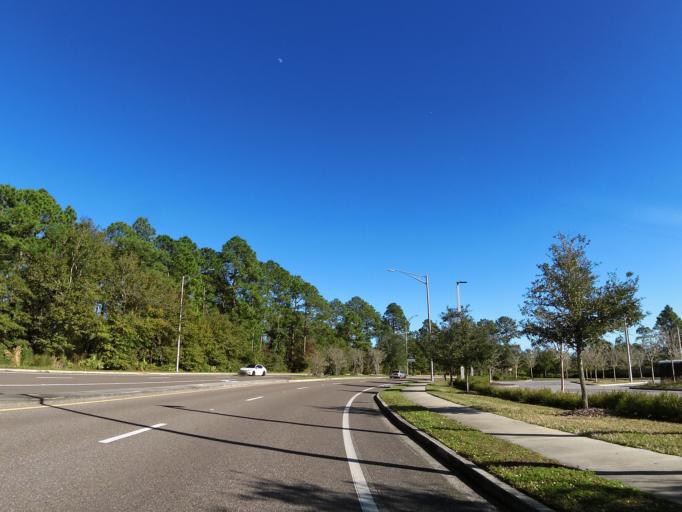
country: US
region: Florida
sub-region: Duval County
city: Jacksonville
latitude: 30.2472
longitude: -81.5542
